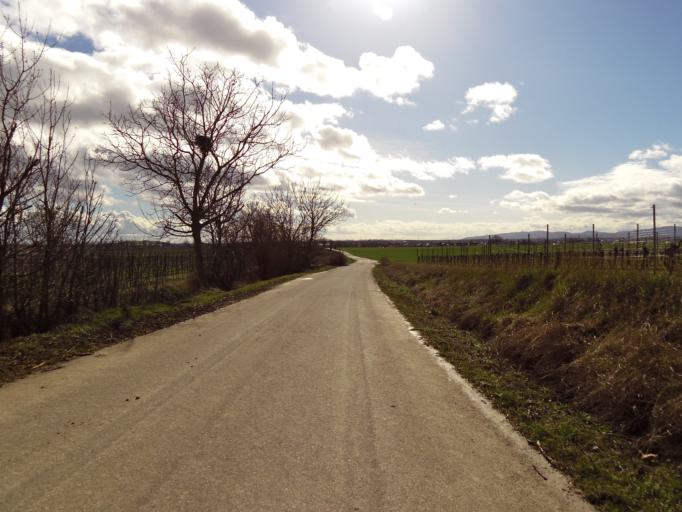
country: DE
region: Rheinland-Pfalz
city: Dirmstein
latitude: 49.5775
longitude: 8.2615
